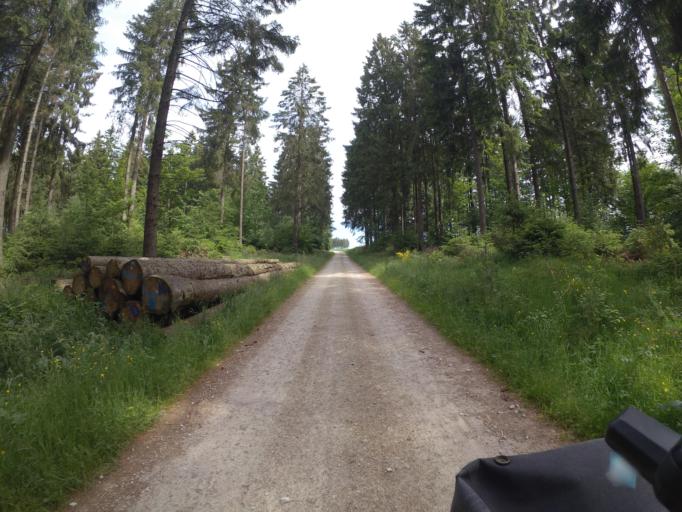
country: DE
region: Rheinland-Pfalz
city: Damflos
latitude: 49.6838
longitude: 6.9773
